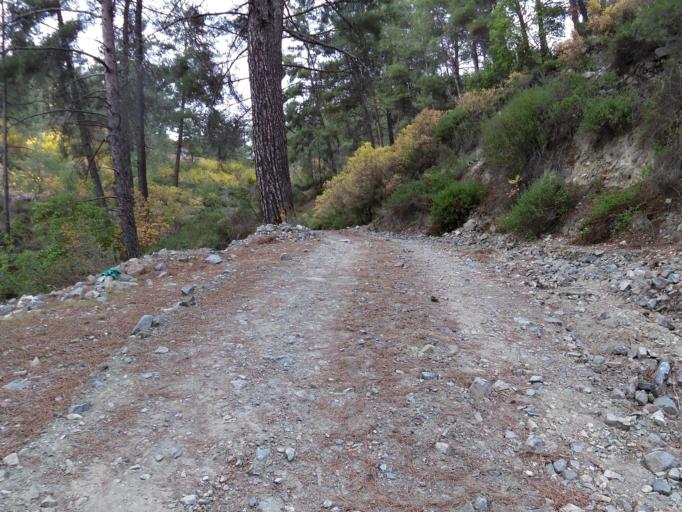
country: CY
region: Limassol
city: Kyperounta
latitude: 34.9299
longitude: 32.9430
